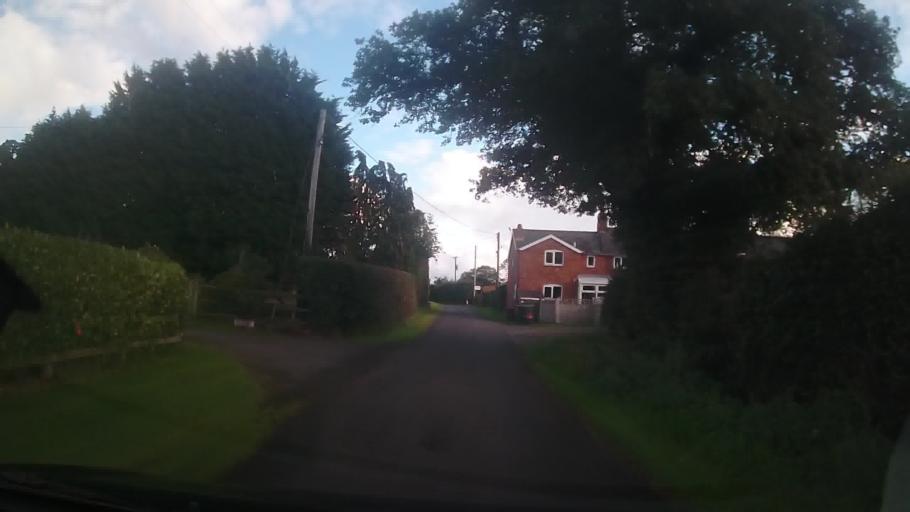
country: GB
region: England
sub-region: Shropshire
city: Wem
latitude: 52.8867
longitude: -2.7447
